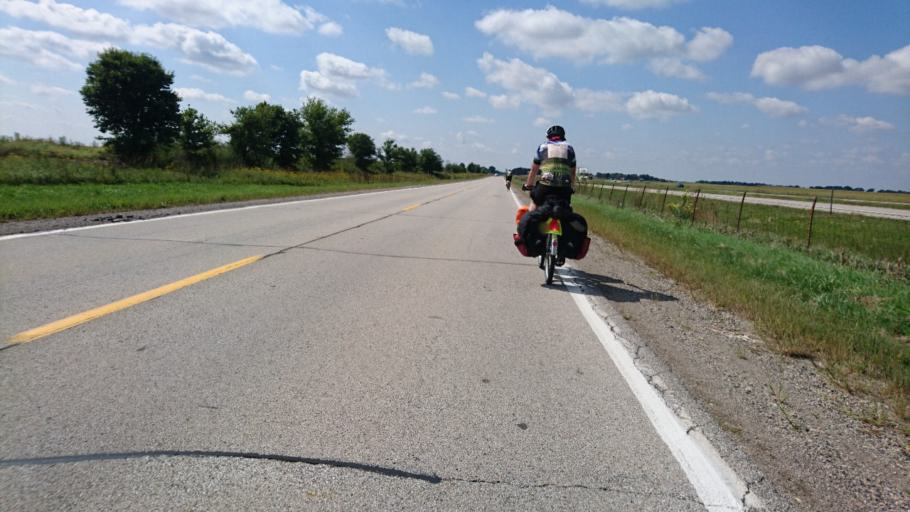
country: US
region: Illinois
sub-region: McLean County
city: Lexington
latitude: 40.5923
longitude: -88.8567
